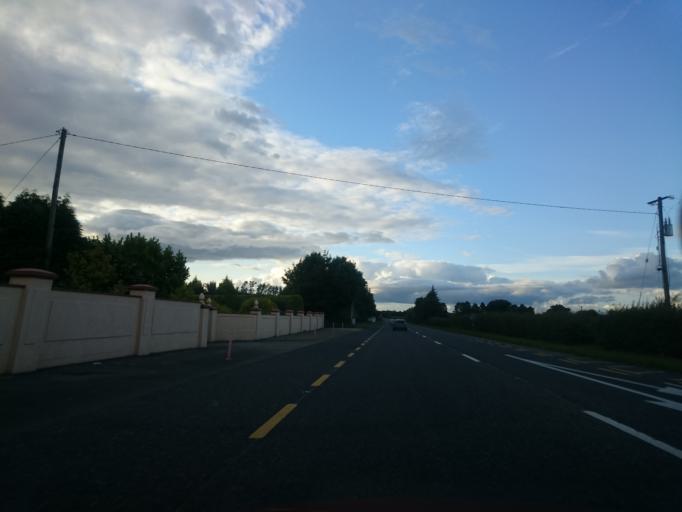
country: IE
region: Leinster
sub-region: Loch Garman
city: Castlebridge
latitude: 52.3946
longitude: -6.5198
